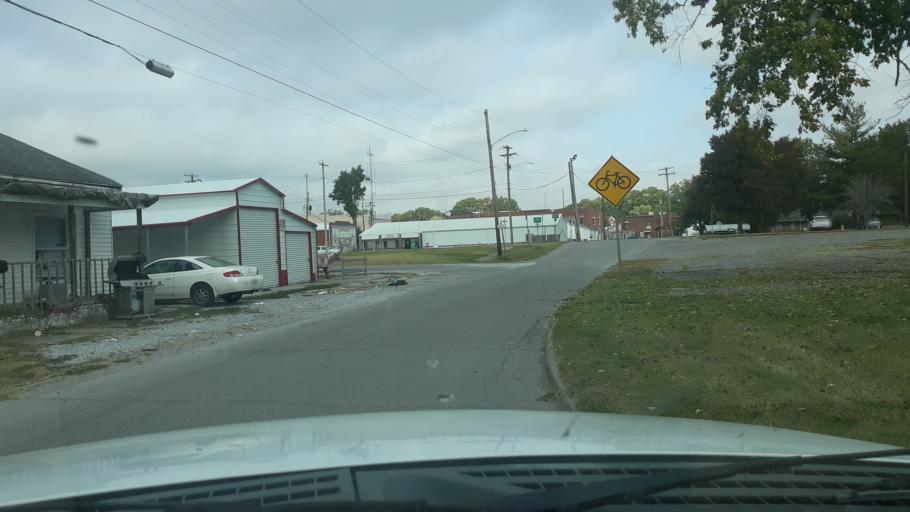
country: US
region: Illinois
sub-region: Saline County
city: Eldorado
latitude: 37.8126
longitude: -88.4361
